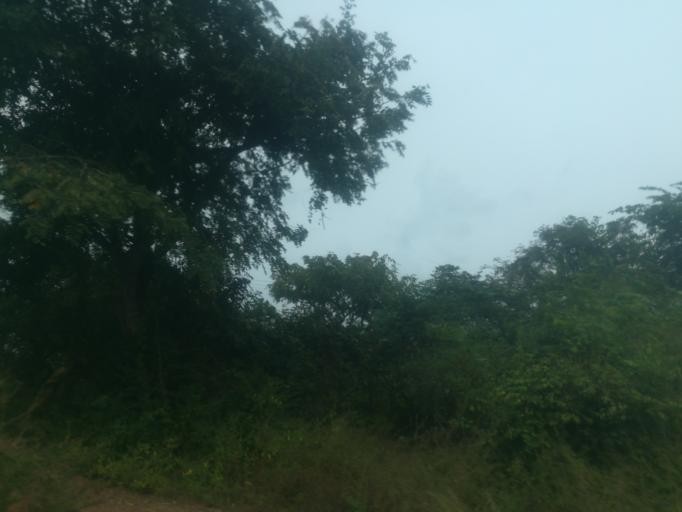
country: NG
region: Ogun
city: Ayetoro
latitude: 7.3476
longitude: 3.0553
